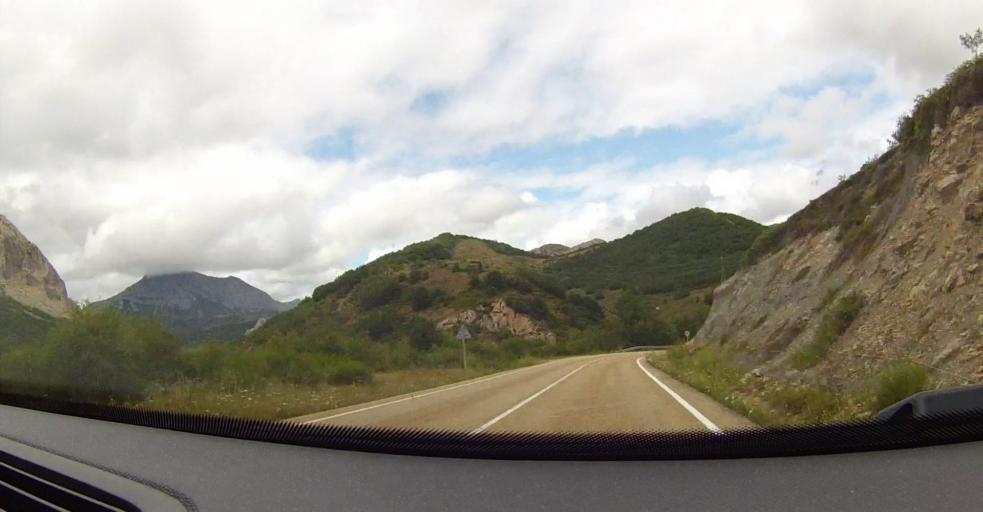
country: ES
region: Castille and Leon
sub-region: Provincia de Leon
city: Reyero
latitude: 42.9470
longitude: -5.2437
